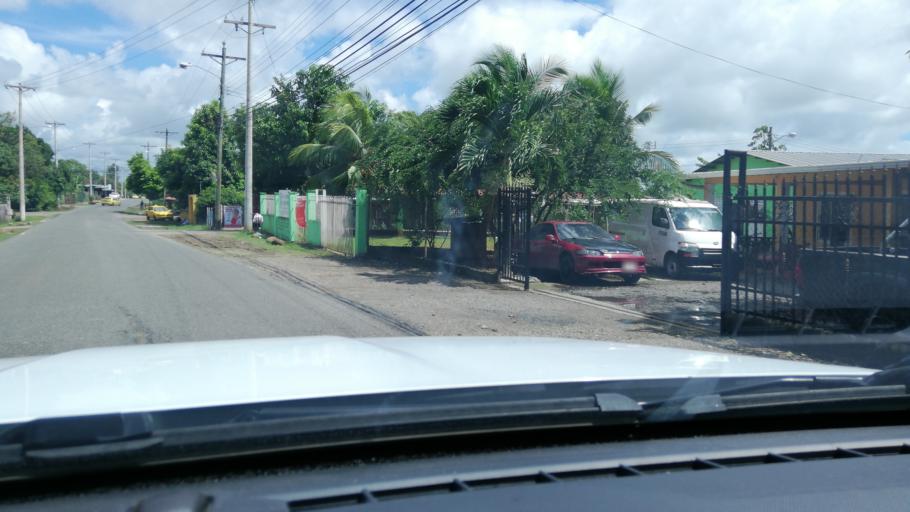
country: PA
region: Panama
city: Cabra Numero Uno
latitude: 9.1091
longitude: -79.3419
